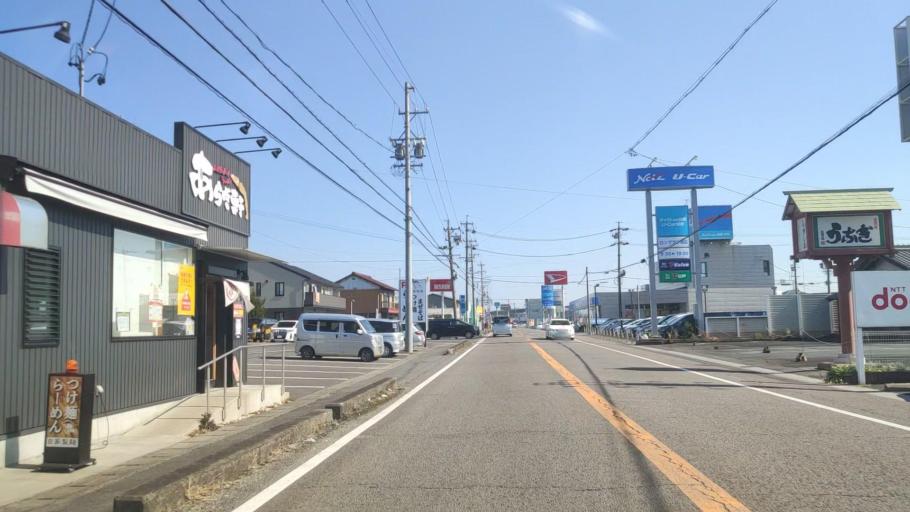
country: JP
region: Gifu
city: Kasamatsucho
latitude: 35.3916
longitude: 136.7981
